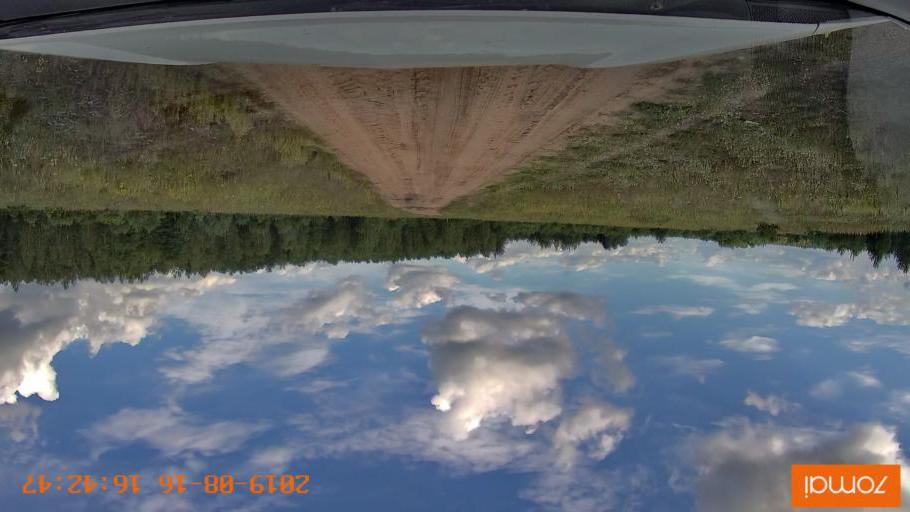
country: BY
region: Mogilev
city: Asipovichy
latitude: 53.2415
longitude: 28.7769
